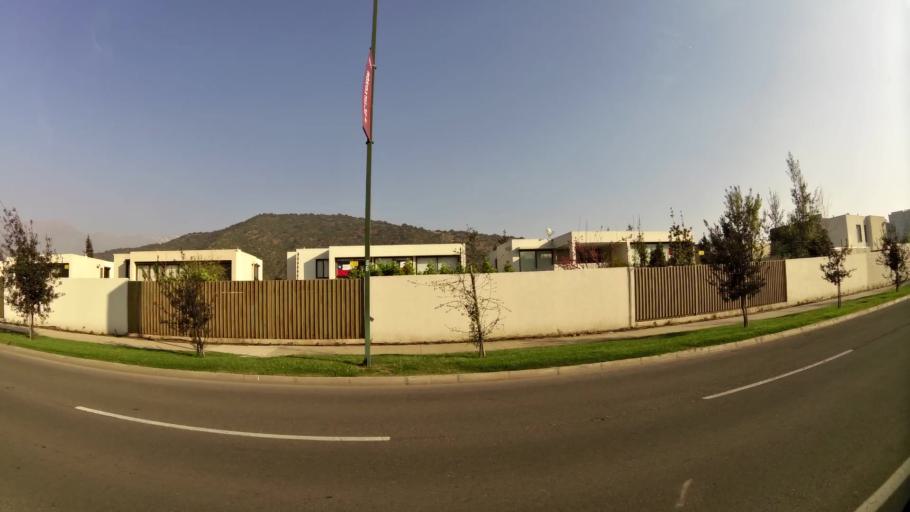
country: CL
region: Santiago Metropolitan
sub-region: Provincia de Santiago
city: Villa Presidente Frei, Nunoa, Santiago, Chile
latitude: -33.3612
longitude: -70.5402
